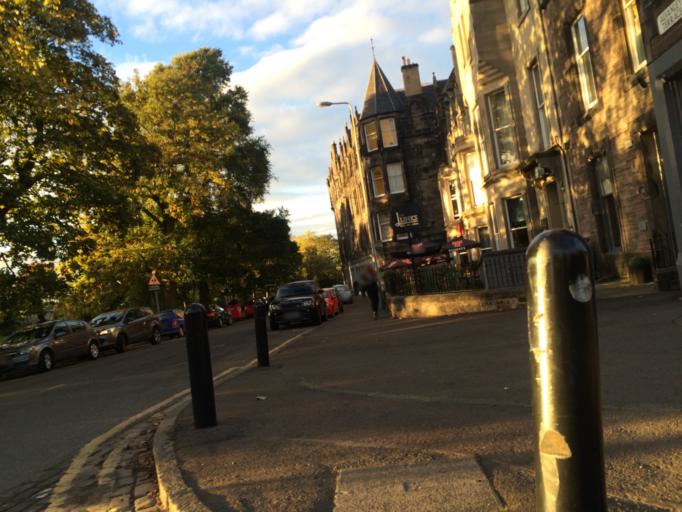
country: GB
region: Scotland
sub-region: Edinburgh
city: Edinburgh
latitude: 55.9371
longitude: -3.2028
